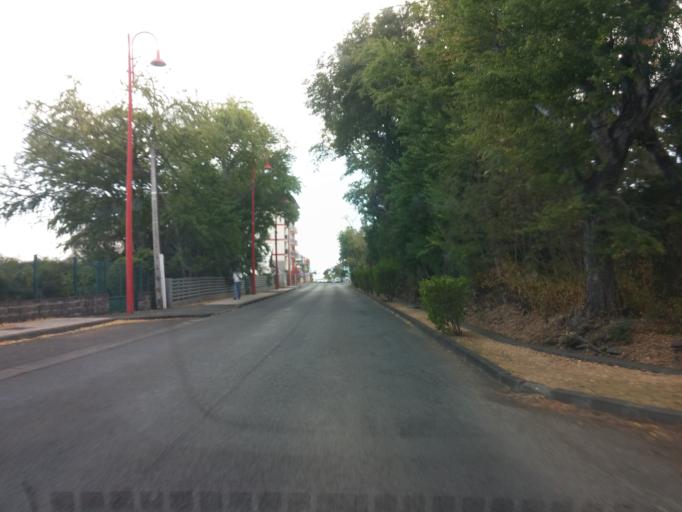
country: RE
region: Reunion
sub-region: Reunion
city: La Possession
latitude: -20.9343
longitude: 55.3343
